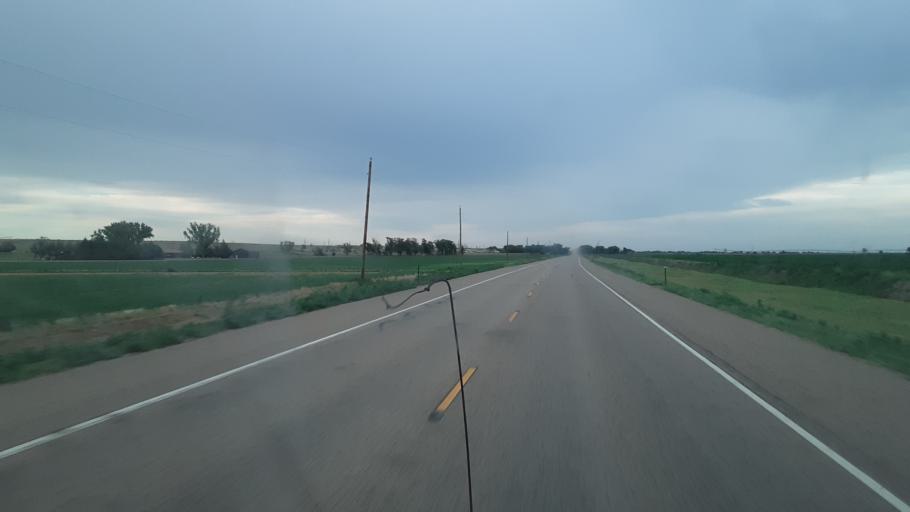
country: US
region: Kansas
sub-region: Hamilton County
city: Syracuse
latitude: 38.0541
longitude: -102.1055
